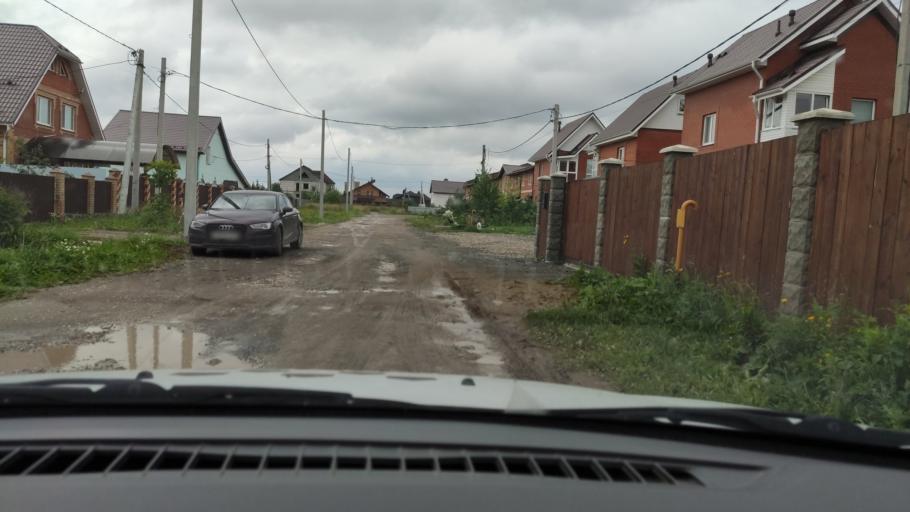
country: RU
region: Perm
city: Perm
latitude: 58.0423
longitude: 56.3787
